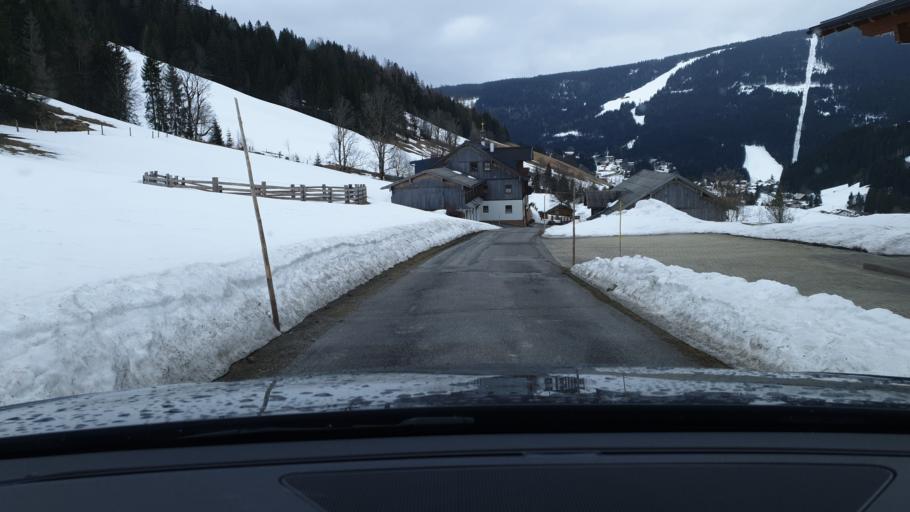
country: AT
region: Salzburg
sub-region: Politischer Bezirk Sankt Johann im Pongau
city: Filzmoos
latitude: 47.4485
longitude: 13.5220
